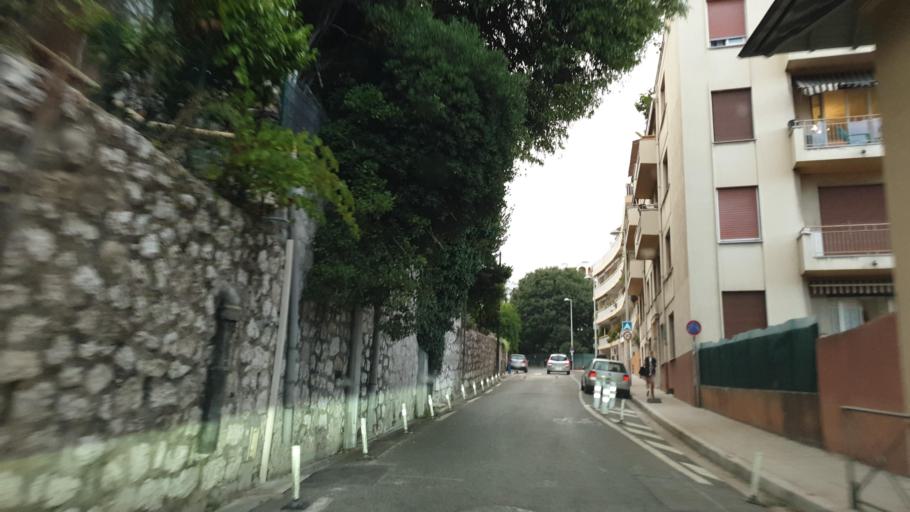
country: FR
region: Provence-Alpes-Cote d'Azur
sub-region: Departement des Alpes-Maritimes
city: Nice
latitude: 43.7045
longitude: 7.2788
